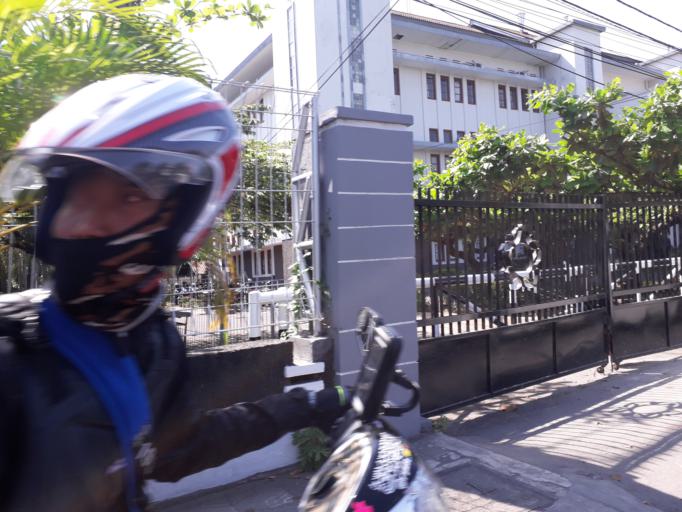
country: ID
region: Daerah Istimewa Yogyakarta
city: Yogyakarta
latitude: -7.7754
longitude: 110.3747
